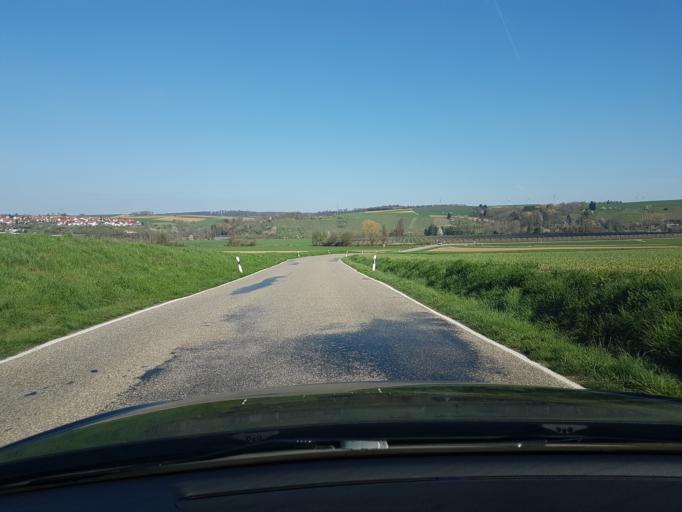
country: DE
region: Baden-Wuerttemberg
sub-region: Regierungsbezirk Stuttgart
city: Neuenstadt am Kocher
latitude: 49.2353
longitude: 9.3824
